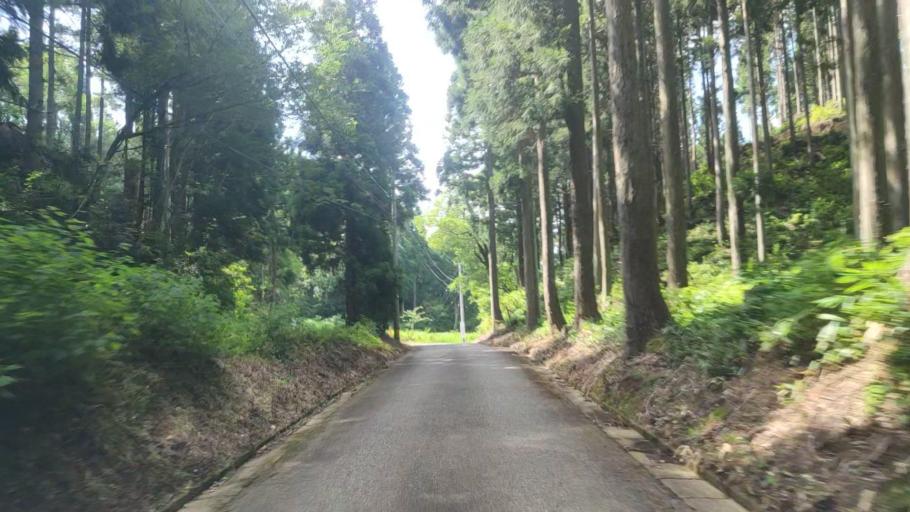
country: JP
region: Ishikawa
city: Komatsu
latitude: 36.2732
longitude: 136.5344
